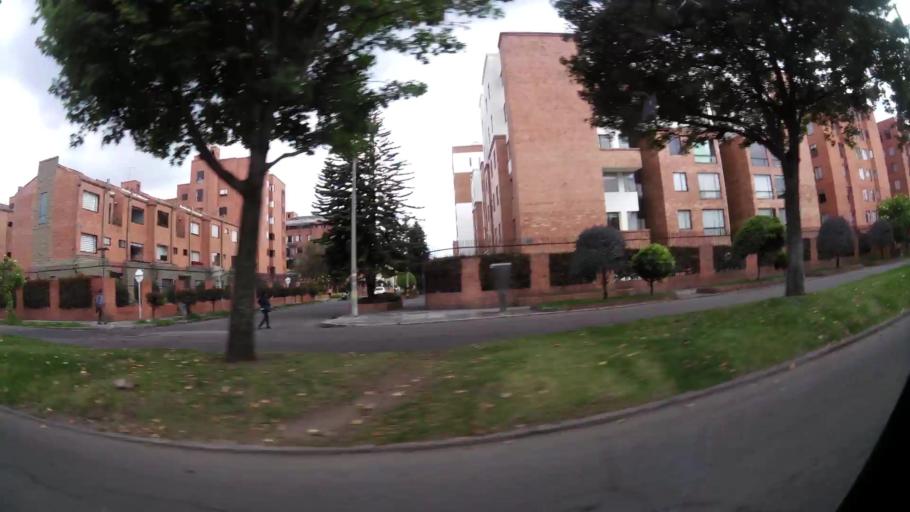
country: CO
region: Bogota D.C.
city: Barrio San Luis
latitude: 4.7299
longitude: -74.0477
